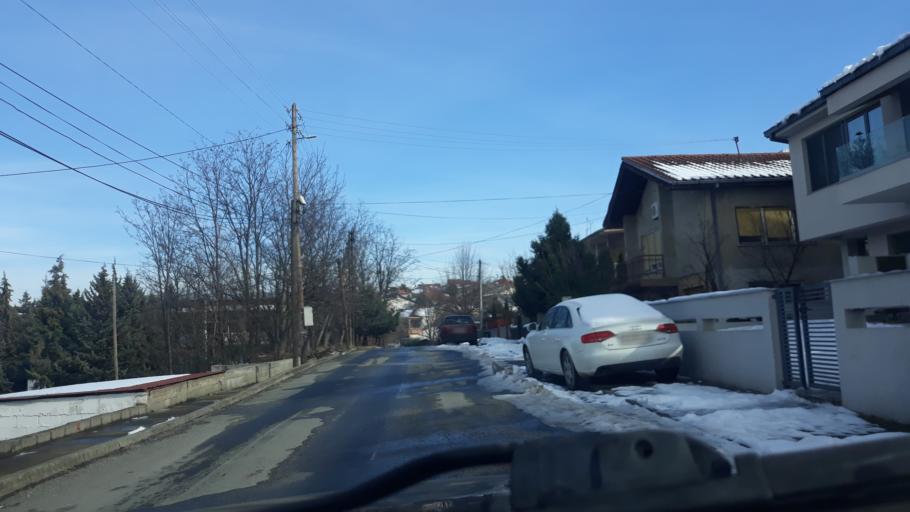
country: MK
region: Negotino
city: Negotino
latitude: 41.4811
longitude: 22.0829
